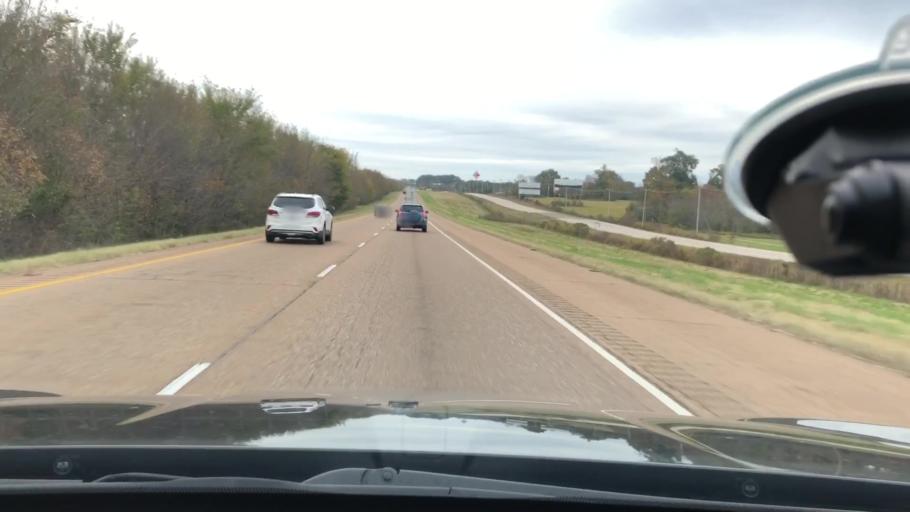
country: US
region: Arkansas
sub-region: Nevada County
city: Prescott
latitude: 33.8203
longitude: -93.4099
